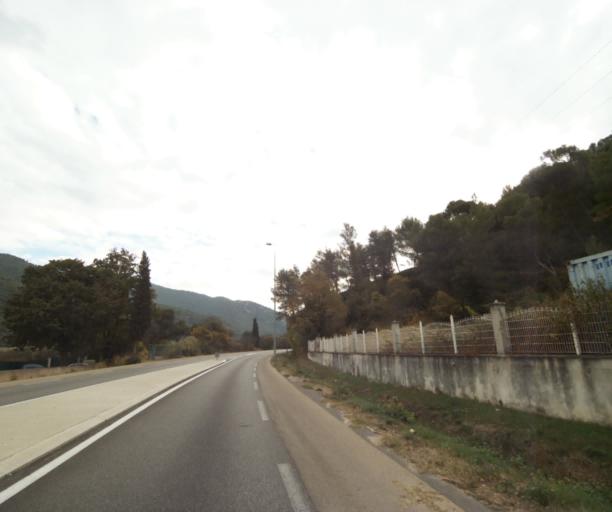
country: FR
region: Provence-Alpes-Cote d'Azur
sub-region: Departement des Bouches-du-Rhone
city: Gemenos
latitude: 43.2768
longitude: 5.6288
